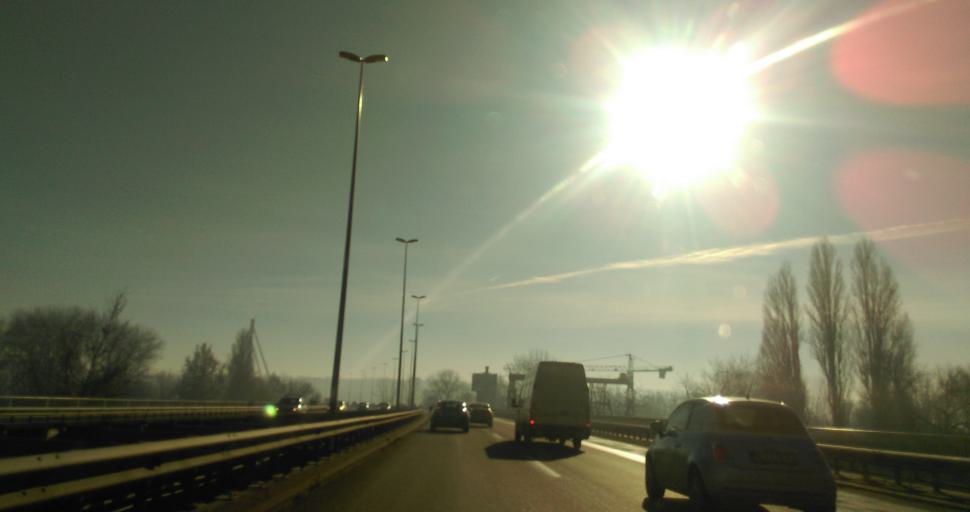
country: RS
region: Autonomna Pokrajina Vojvodina
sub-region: Juznobacki Okrug
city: Novi Sad
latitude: 45.2393
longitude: 19.8440
